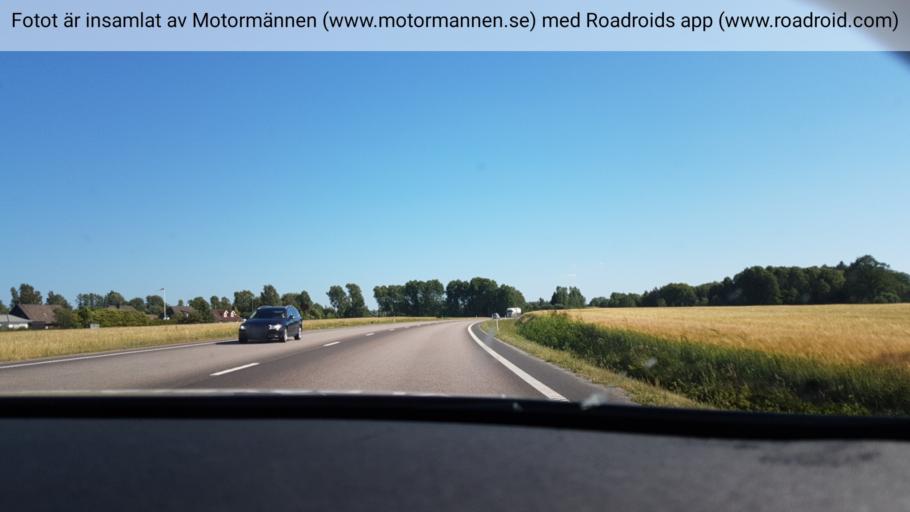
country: SE
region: Vaestra Goetaland
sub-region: Skara Kommun
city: Skara
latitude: 58.3910
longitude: 13.4103
